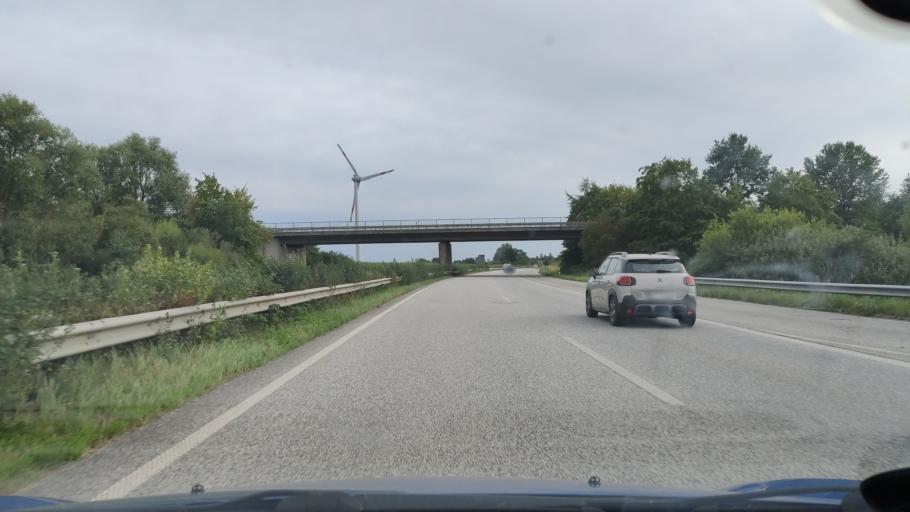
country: DE
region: Schleswig-Holstein
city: Rumpel
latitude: 53.8137
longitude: 10.3249
